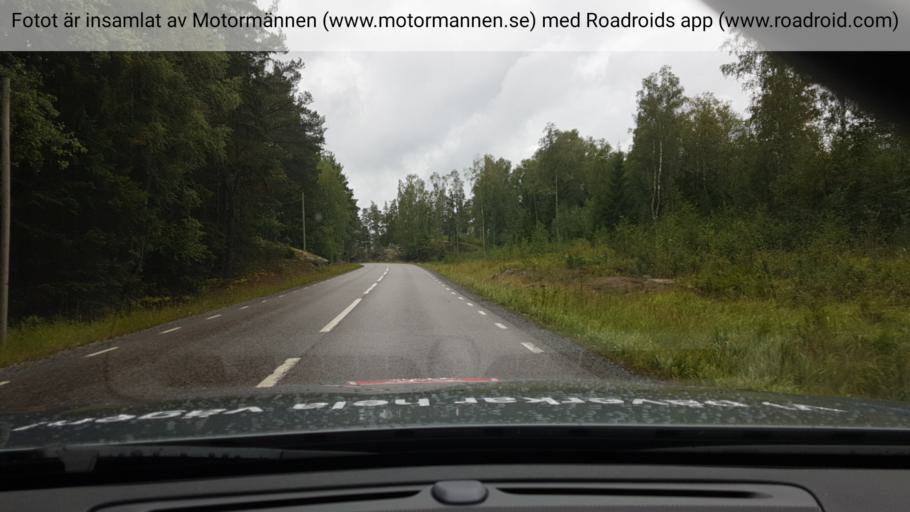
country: SE
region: Stockholm
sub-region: Botkyrka Kommun
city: Tullinge
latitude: 59.1807
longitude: 17.9286
